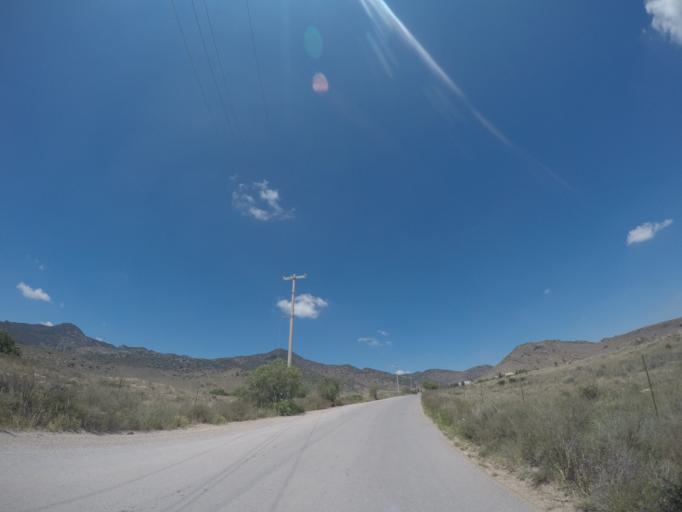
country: MX
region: San Luis Potosi
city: La Pila
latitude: 22.0145
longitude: -100.9127
